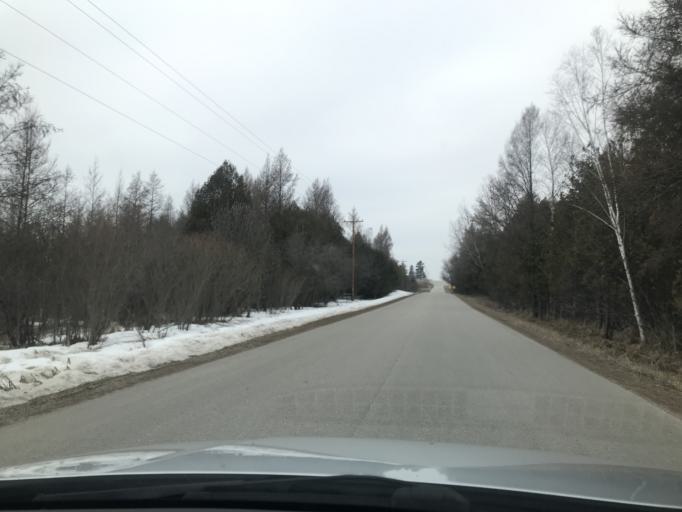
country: US
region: Wisconsin
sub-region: Marinette County
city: Peshtigo
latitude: 45.0276
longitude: -87.8644
